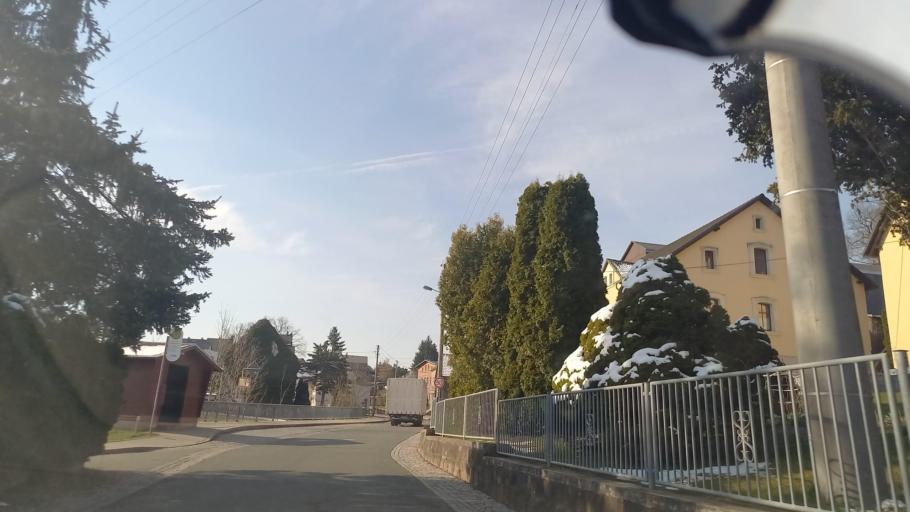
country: DE
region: Saxony
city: Stutzengrun
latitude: 50.5700
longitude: 12.4815
